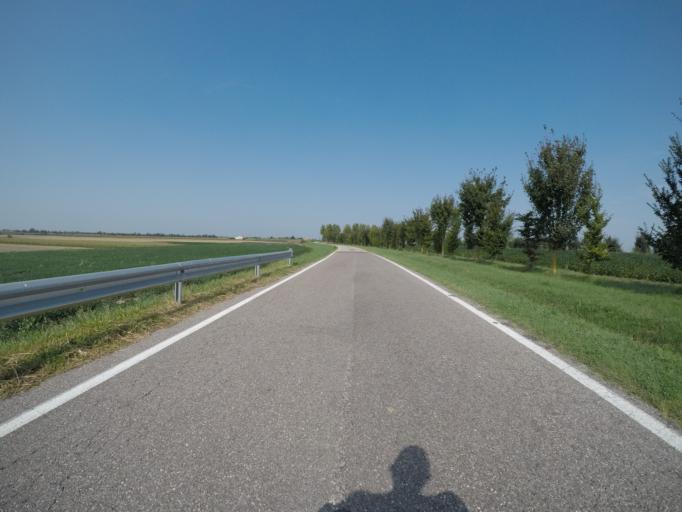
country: IT
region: Veneto
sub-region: Provincia di Rovigo
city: Villanova del Ghebbo Canton
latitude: 45.0638
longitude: 11.6223
